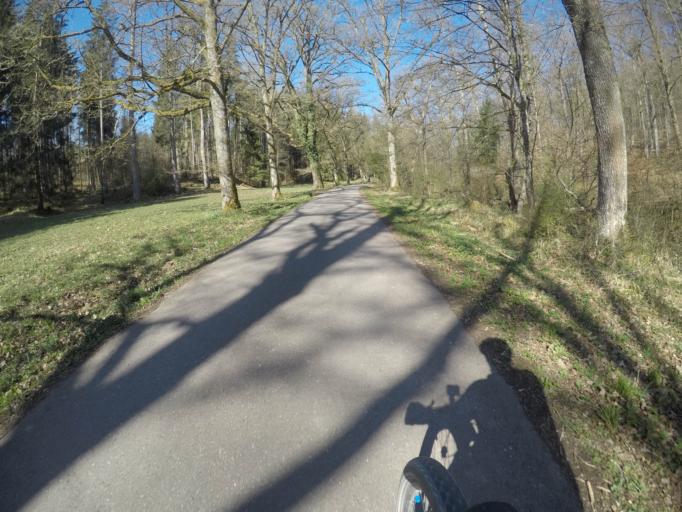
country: DE
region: Baden-Wuerttemberg
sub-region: Tuebingen Region
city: Tuebingen
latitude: 48.5604
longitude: 9.0022
